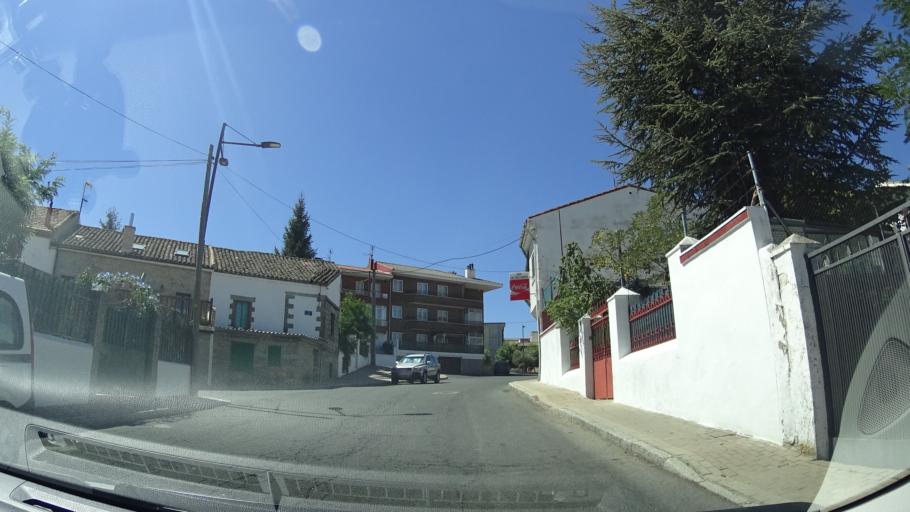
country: ES
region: Castille and Leon
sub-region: Provincia de Avila
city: Las Navas del Marques
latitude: 40.6010
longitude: -4.3347
